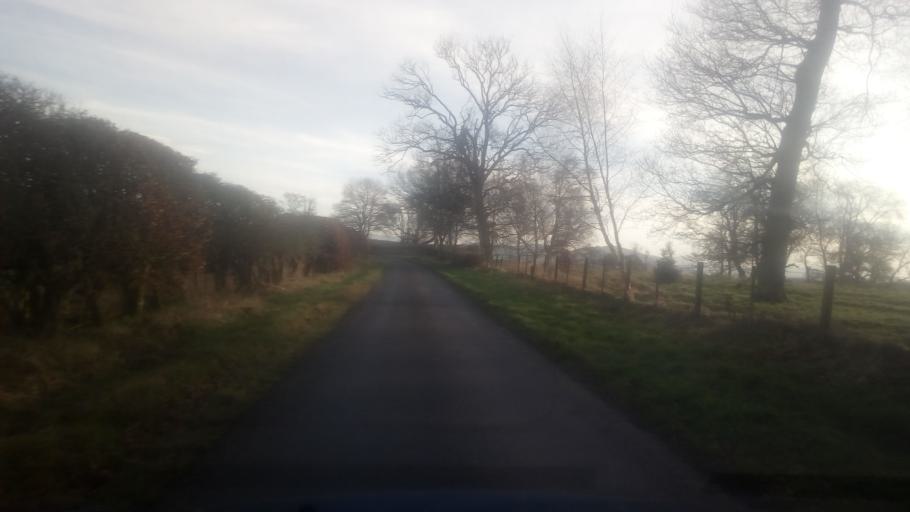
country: GB
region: Scotland
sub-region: The Scottish Borders
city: Jedburgh
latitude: 55.4409
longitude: -2.6303
